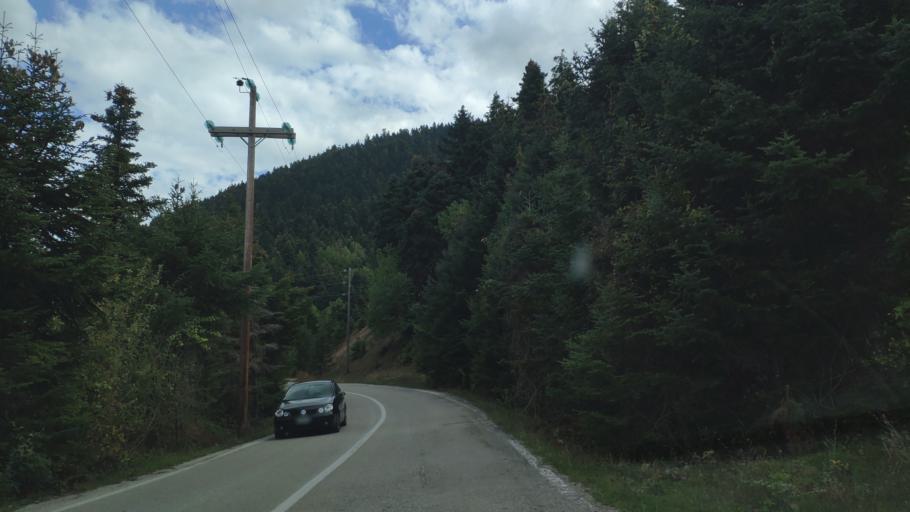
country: GR
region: Central Greece
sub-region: Nomos Fthiotidos
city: Stavros
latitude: 38.7307
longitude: 22.3530
